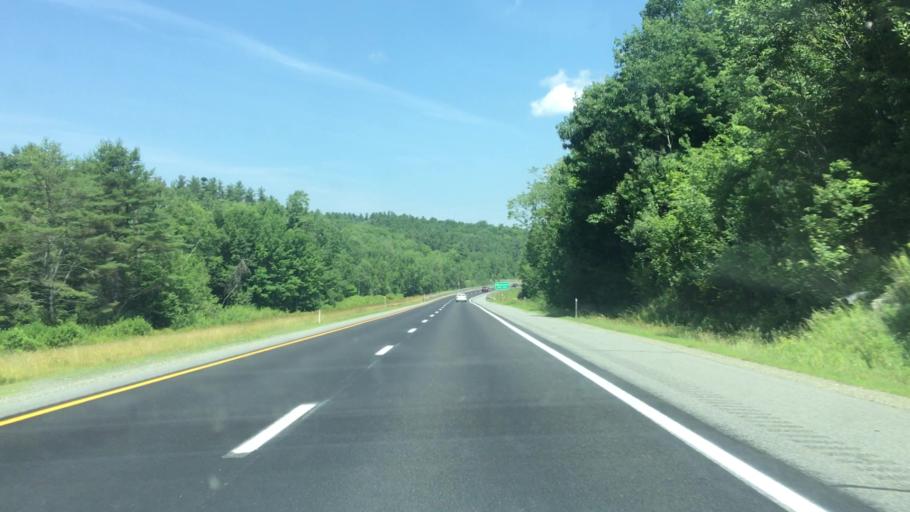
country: US
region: New Hampshire
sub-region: Grafton County
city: Enfield
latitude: 43.5876
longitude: -72.1654
